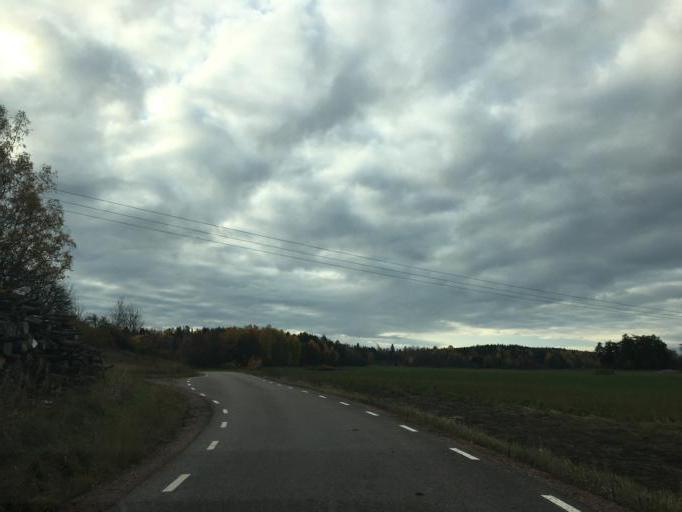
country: SE
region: Vaestmanland
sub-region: Vasteras
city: Vasteras
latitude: 59.5814
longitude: 16.4796
